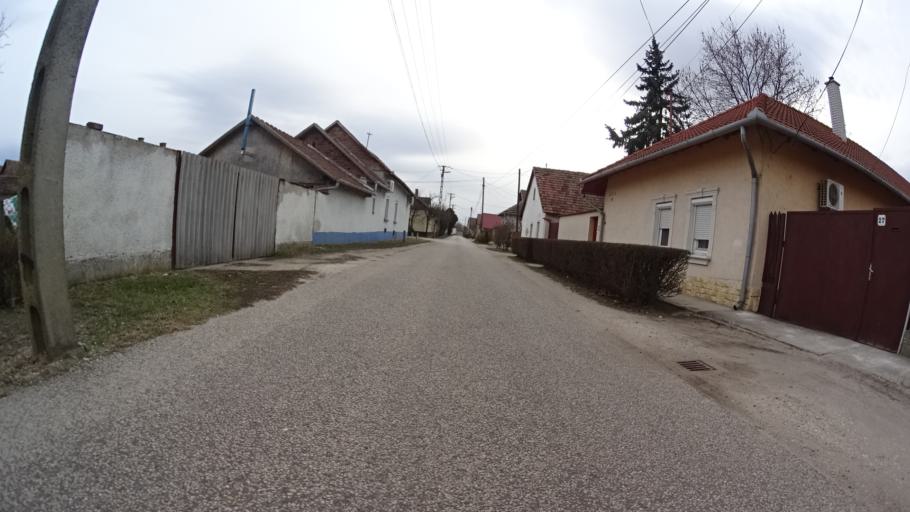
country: HU
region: Bacs-Kiskun
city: Tiszakecske
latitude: 46.9377
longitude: 20.0865
